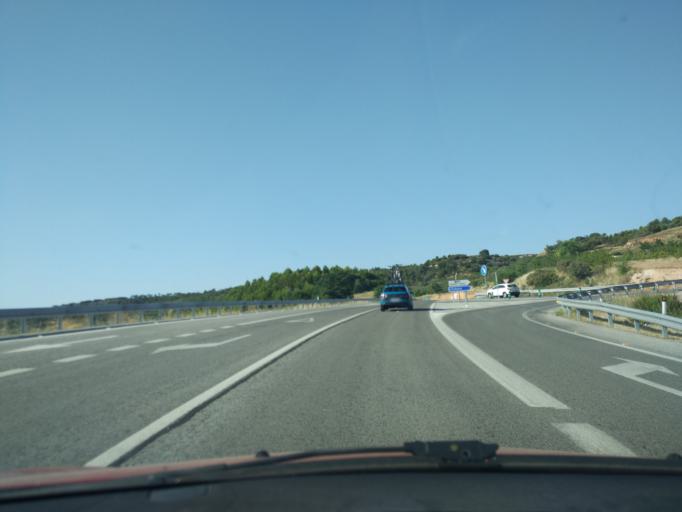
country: ES
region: Madrid
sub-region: Provincia de Madrid
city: Villar del Olmo
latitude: 40.3402
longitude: -3.2406
